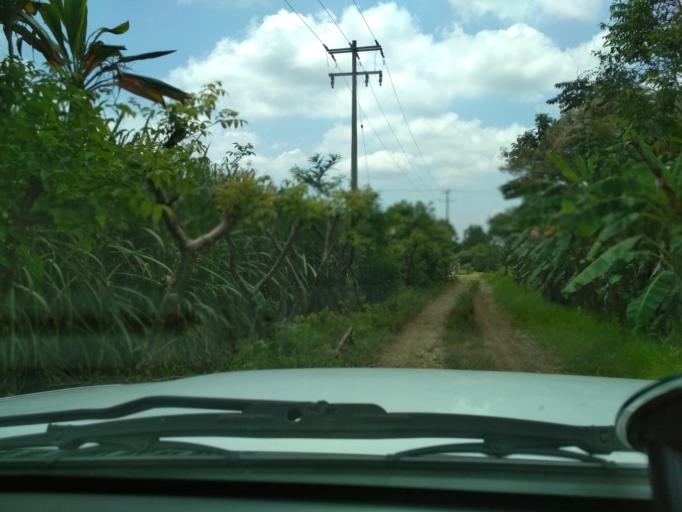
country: MX
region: Veracruz
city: Tocuila
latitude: 18.9563
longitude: -97.0146
